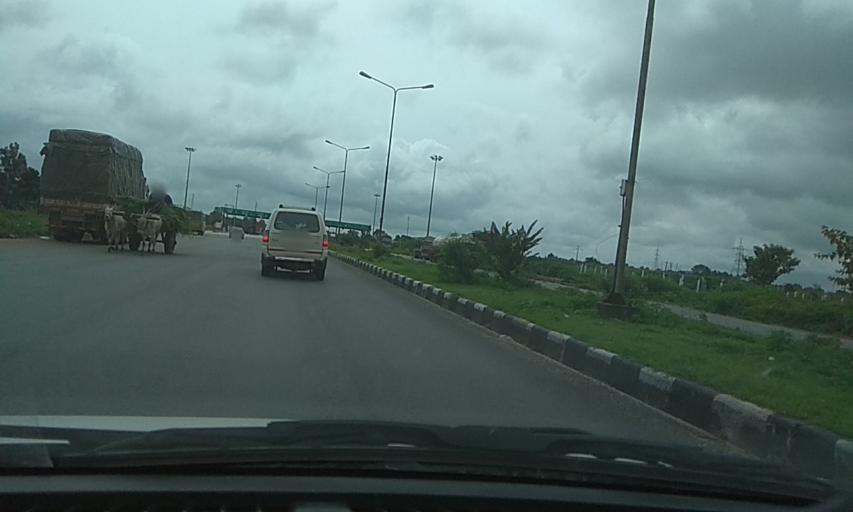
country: IN
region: Karnataka
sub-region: Davanagere
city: Mayakonda
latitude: 14.3763
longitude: 76.1044
